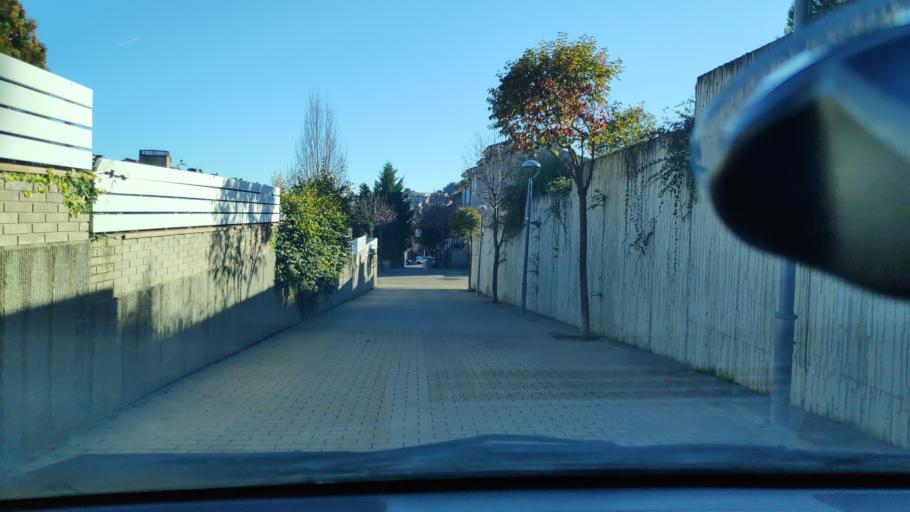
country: ES
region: Catalonia
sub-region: Provincia de Barcelona
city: Sant Quirze del Valles
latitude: 41.5289
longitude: 2.0684
